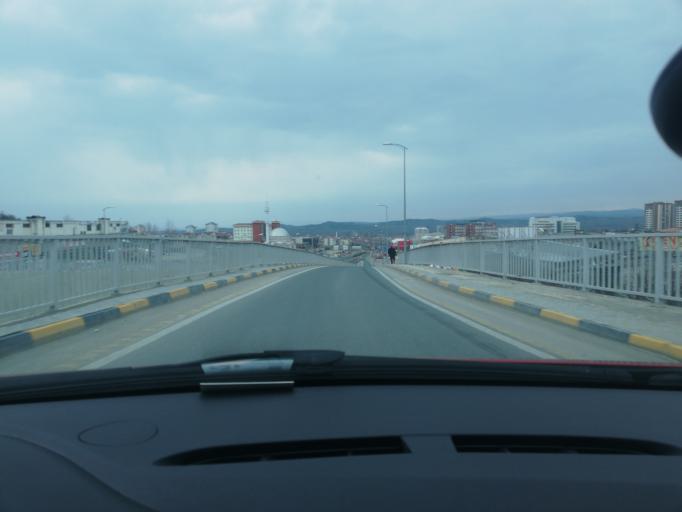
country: TR
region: Kastamonu
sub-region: Cide
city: Kastamonu
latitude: 41.4201
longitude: 33.7785
